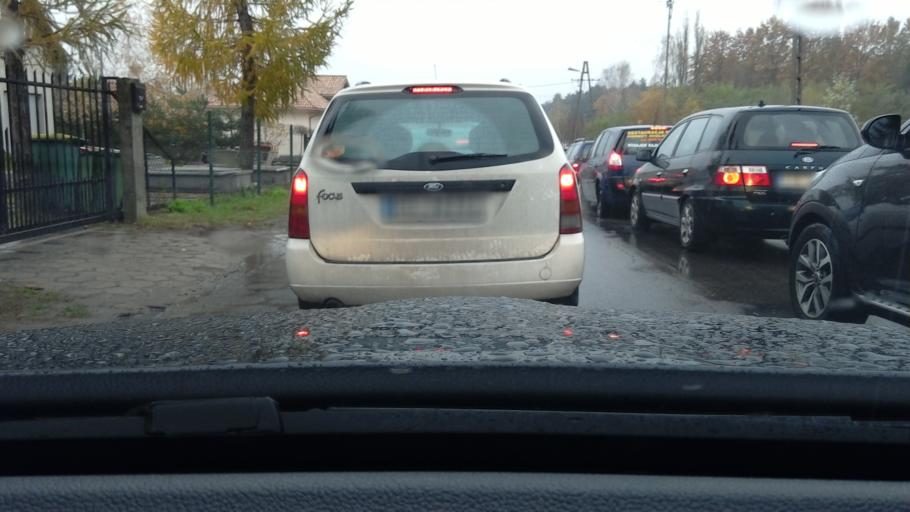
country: PL
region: Lodz Voivodeship
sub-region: Skierniewice
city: Skierniewice
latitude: 51.9406
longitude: 20.1549
